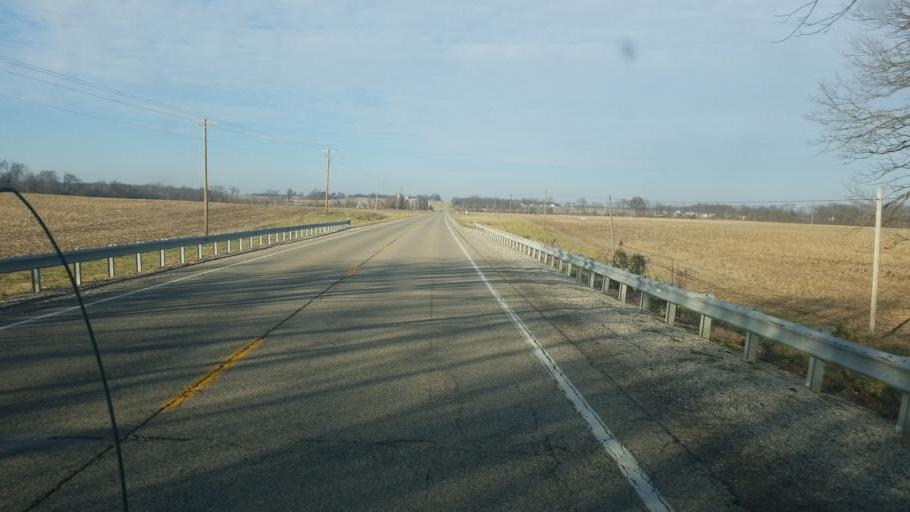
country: US
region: Illinois
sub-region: Lawrence County
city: Lawrenceville
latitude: 38.6383
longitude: -87.6943
